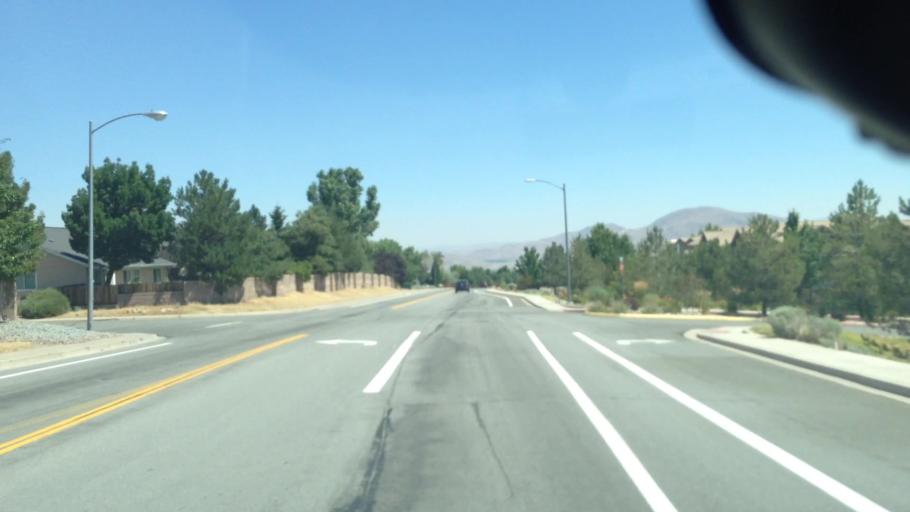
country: US
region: Nevada
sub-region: Washoe County
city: Sparks
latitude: 39.3957
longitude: -119.7673
